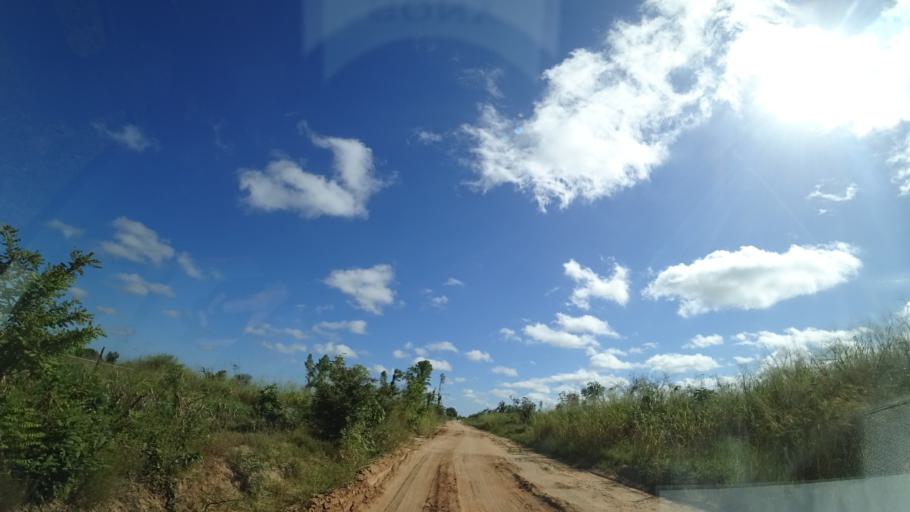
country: MZ
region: Sofala
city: Dondo
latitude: -19.4193
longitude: 34.7108
